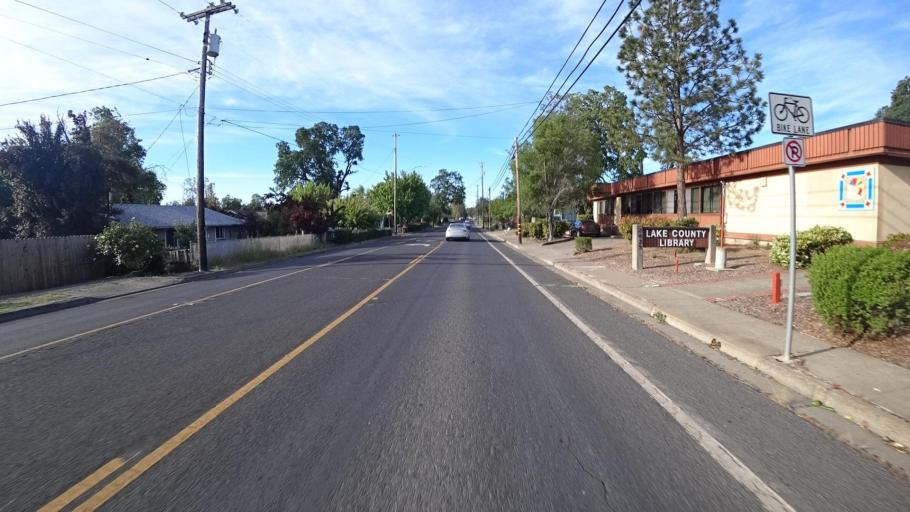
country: US
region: California
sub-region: Lake County
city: Lakeport
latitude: 39.0517
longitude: -122.9171
